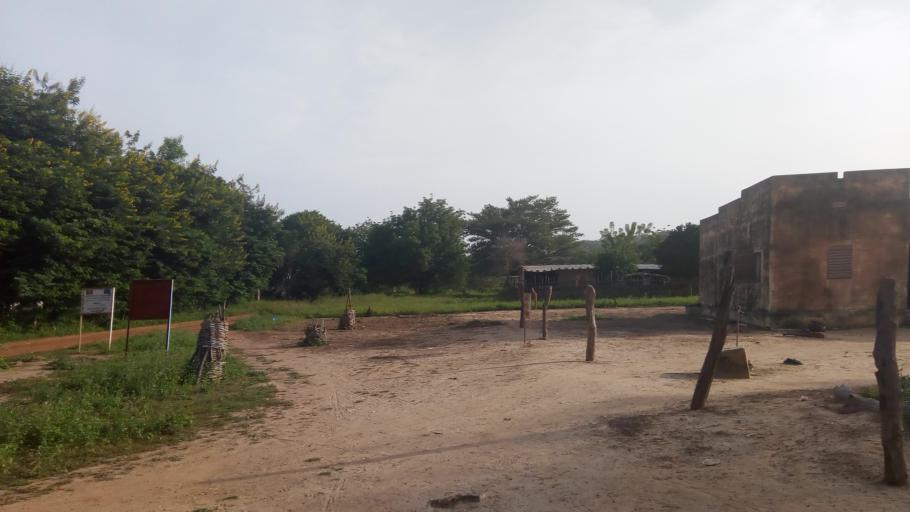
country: ML
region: Kayes
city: Kita
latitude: 13.1306
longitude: -8.8312
